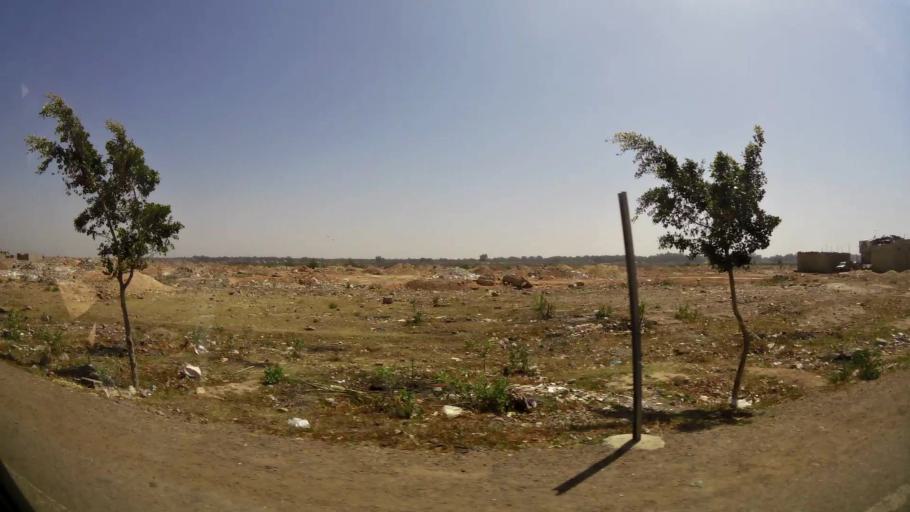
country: MA
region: Souss-Massa-Draa
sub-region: Inezgane-Ait Mellou
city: Inezgane
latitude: 30.3436
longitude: -9.5447
